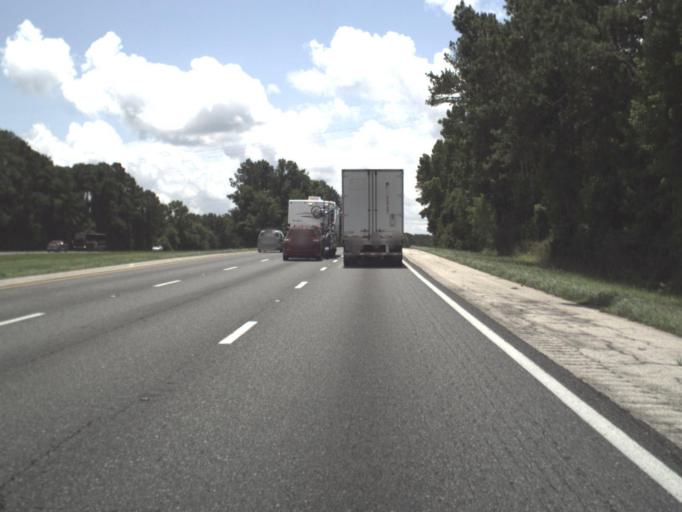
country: US
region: Florida
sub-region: Alachua County
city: Alachua
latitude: 29.7419
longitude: -82.4812
